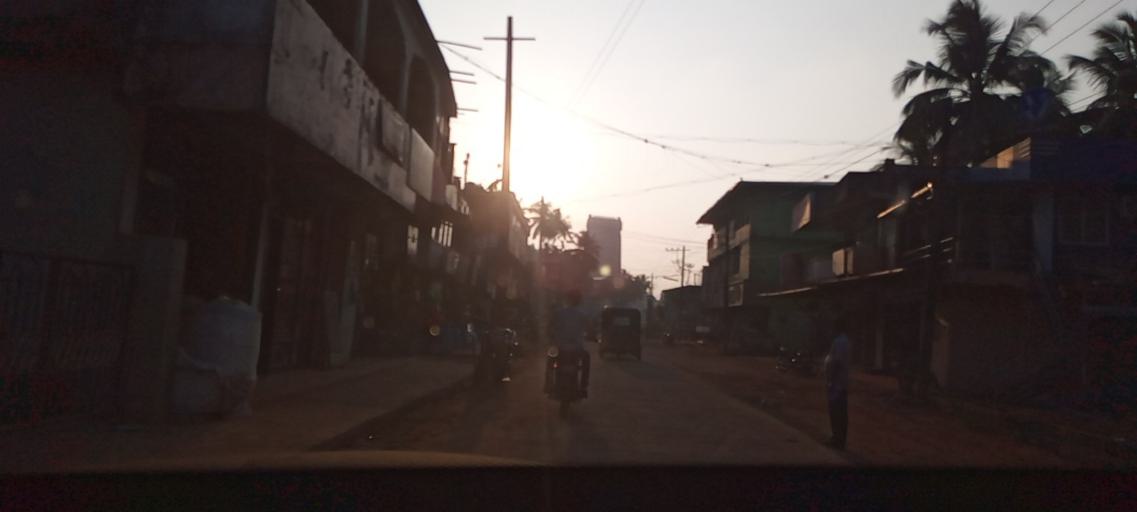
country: IN
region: Karnataka
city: Murudeshwara
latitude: 14.0949
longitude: 74.4907
